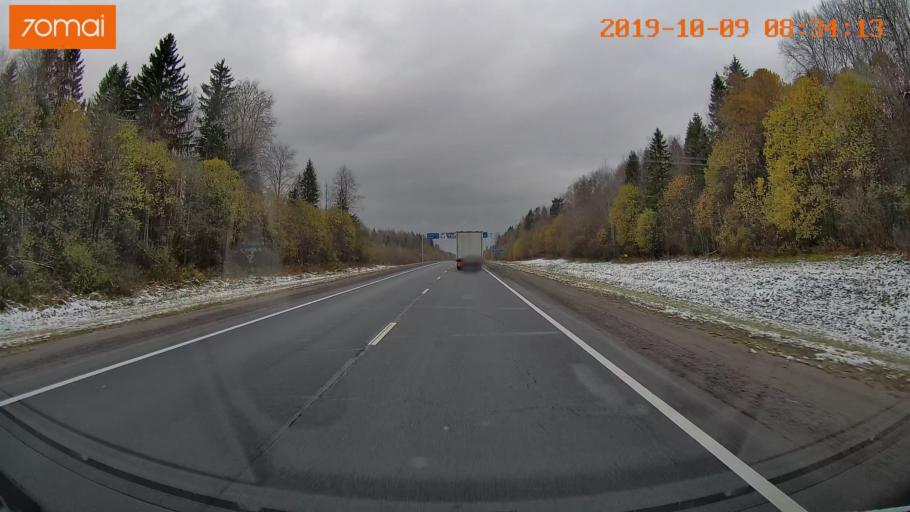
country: RU
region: Vologda
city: Gryazovets
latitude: 58.8937
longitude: 40.1870
